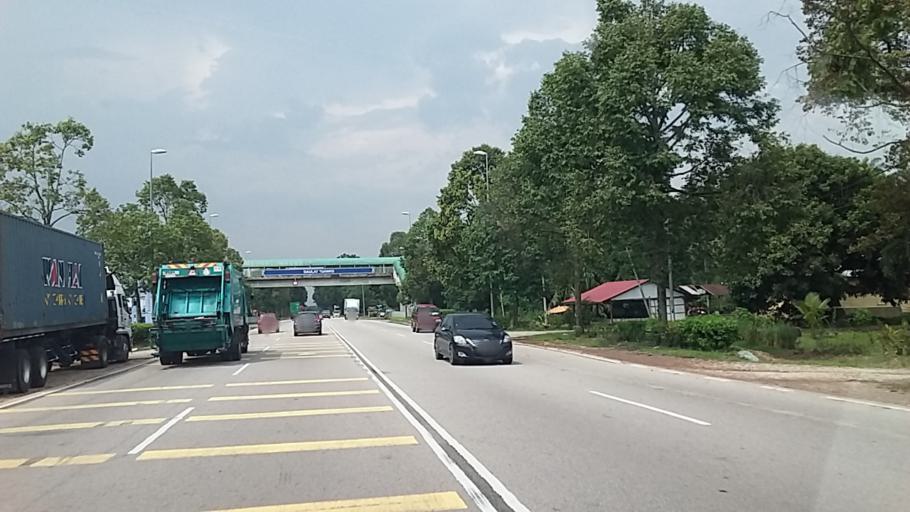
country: MY
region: Johor
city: Parit Raja
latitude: 1.8707
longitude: 103.1280
